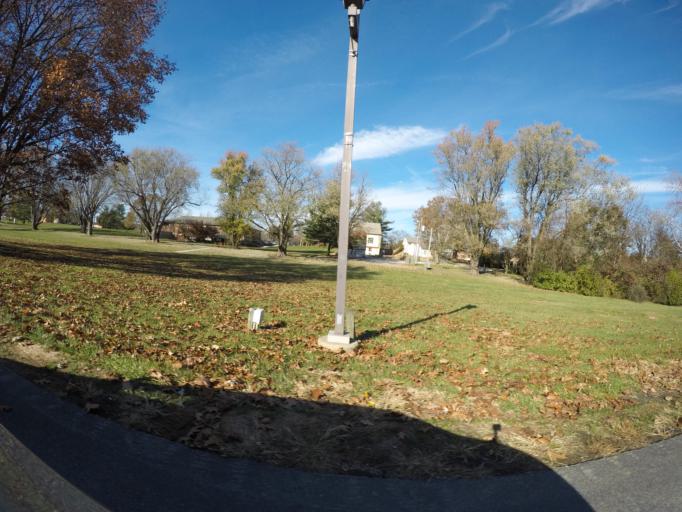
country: US
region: Pennsylvania
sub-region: Chester County
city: Caln
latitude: 40.0089
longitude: -75.7887
